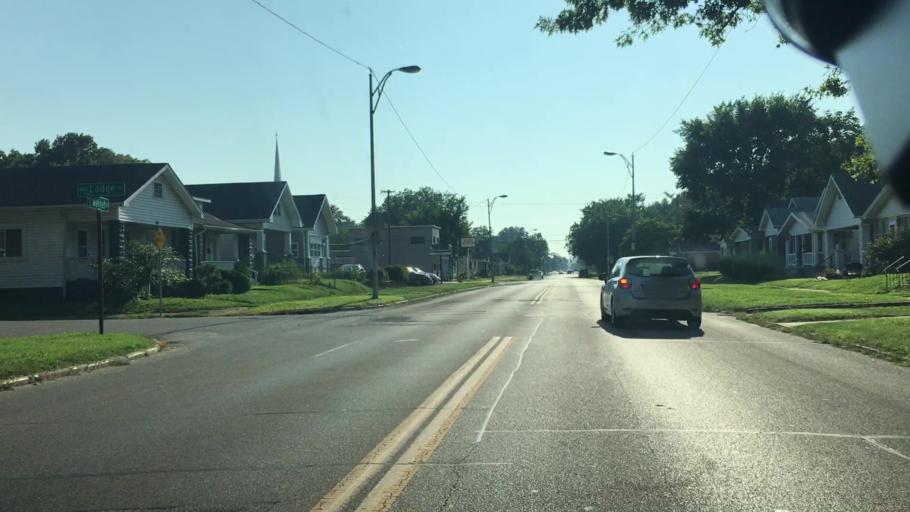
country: US
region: Indiana
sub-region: Vanderburgh County
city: Evansville
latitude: 37.9736
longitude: -87.5381
